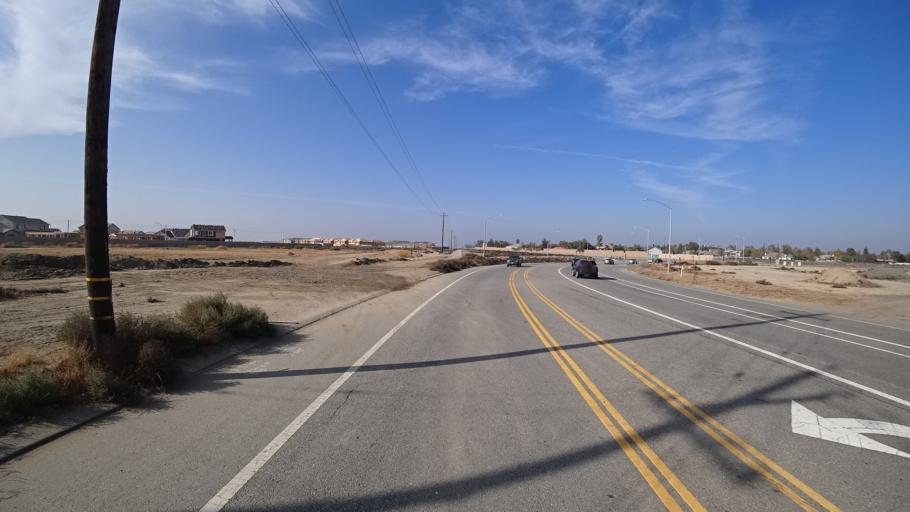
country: US
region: California
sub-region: Kern County
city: Rosedale
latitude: 35.3544
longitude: -119.1737
